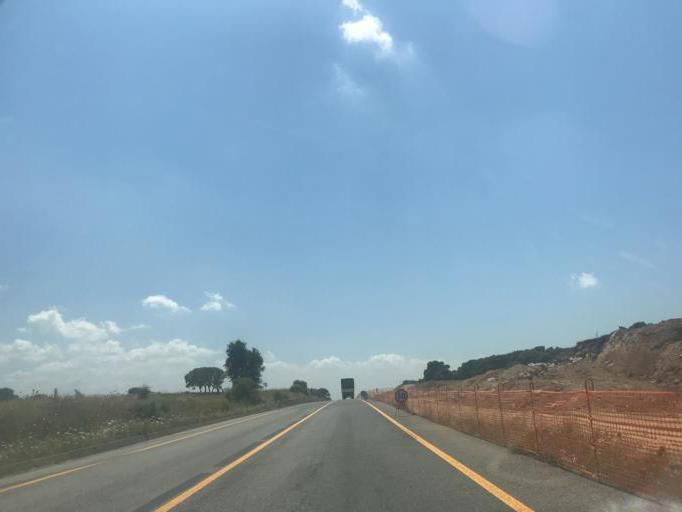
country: IT
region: Sardinia
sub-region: Provincia di Olbia-Tempio
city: Monti
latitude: 40.7885
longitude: 9.2583
